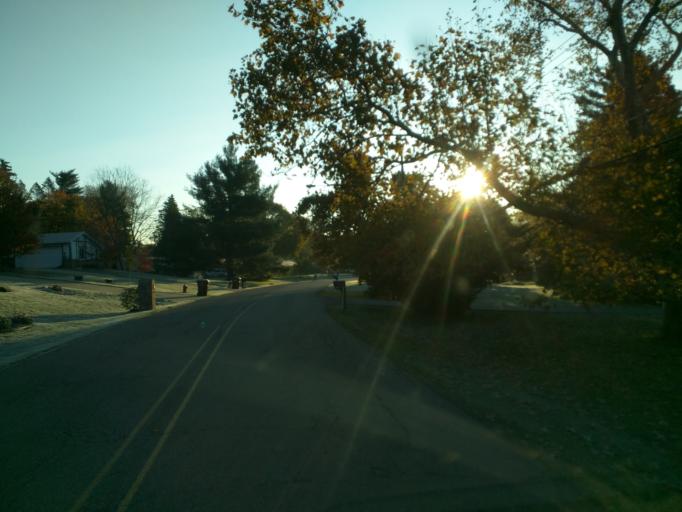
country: US
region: Michigan
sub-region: Ingham County
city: Edgemont Park
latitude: 42.7555
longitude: -84.5980
